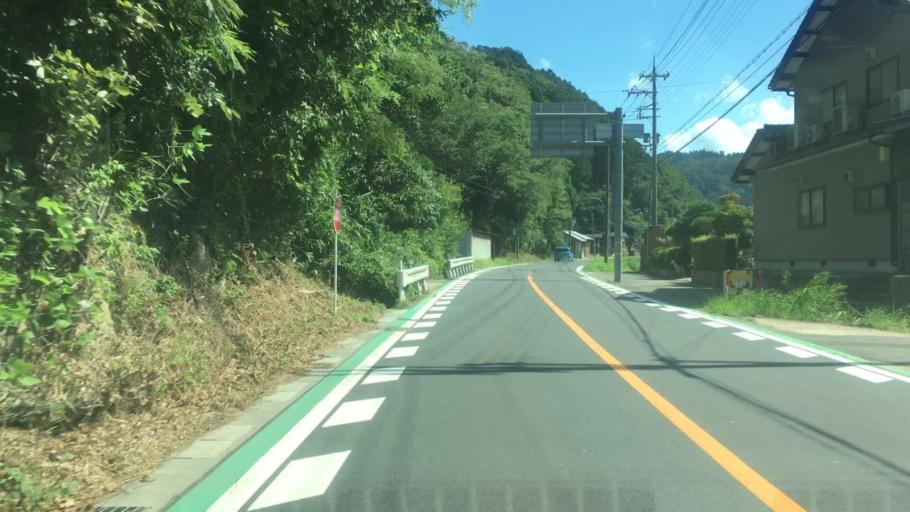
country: JP
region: Hyogo
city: Toyooka
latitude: 35.5980
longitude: 134.9047
